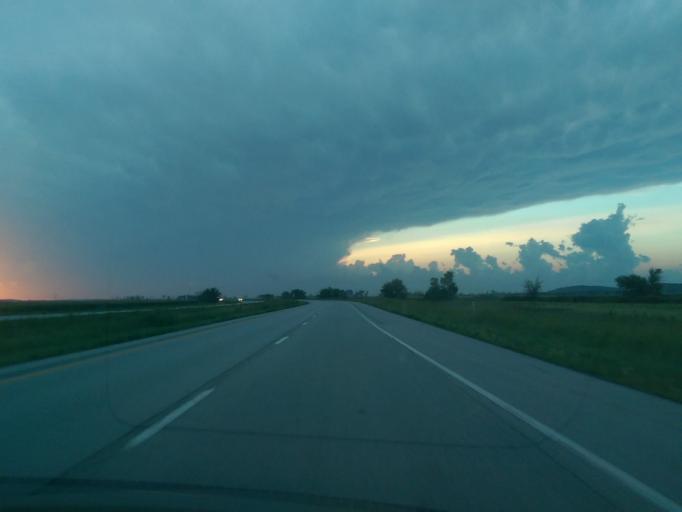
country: US
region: Iowa
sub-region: Fremont County
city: Hamburg
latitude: 40.6053
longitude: -95.6817
